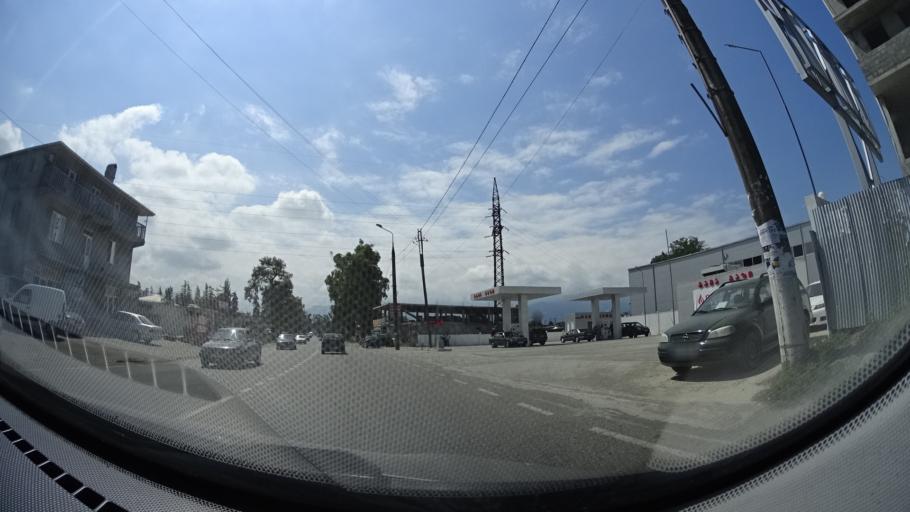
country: GE
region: Ajaria
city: Batumi
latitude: 41.6198
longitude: 41.6171
